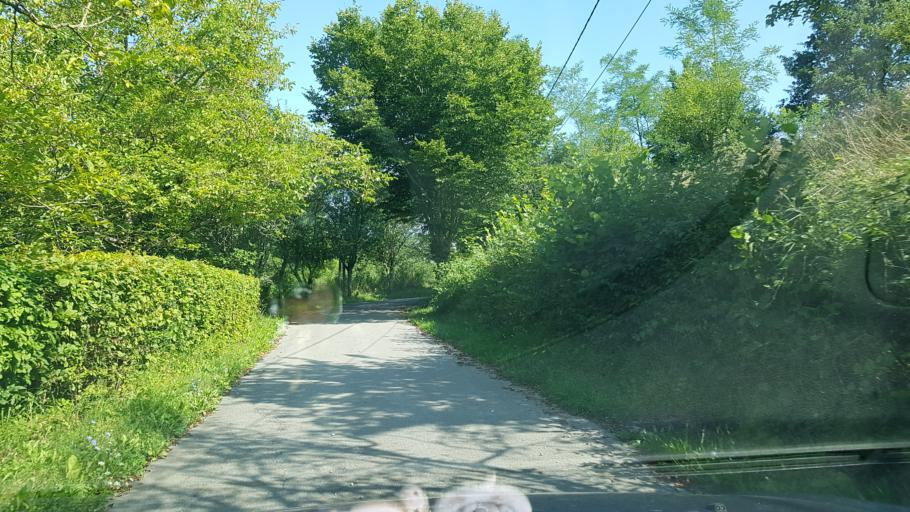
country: SI
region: Pivka
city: Pivka
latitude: 45.6096
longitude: 14.1802
